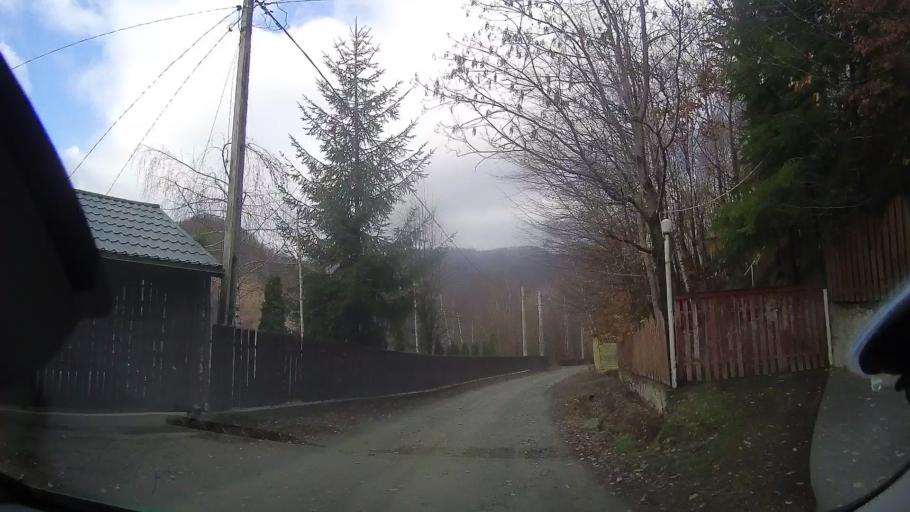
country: RO
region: Cluj
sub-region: Comuna Valea Ierii
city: Valea Ierii
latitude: 46.6812
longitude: 23.3089
